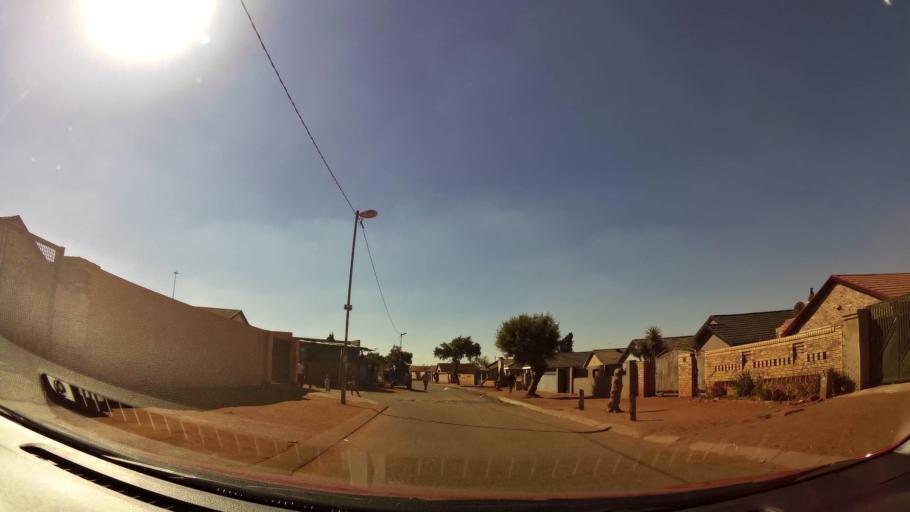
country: ZA
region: Gauteng
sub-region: City of Johannesburg Metropolitan Municipality
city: Soweto
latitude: -26.2481
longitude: 27.8062
